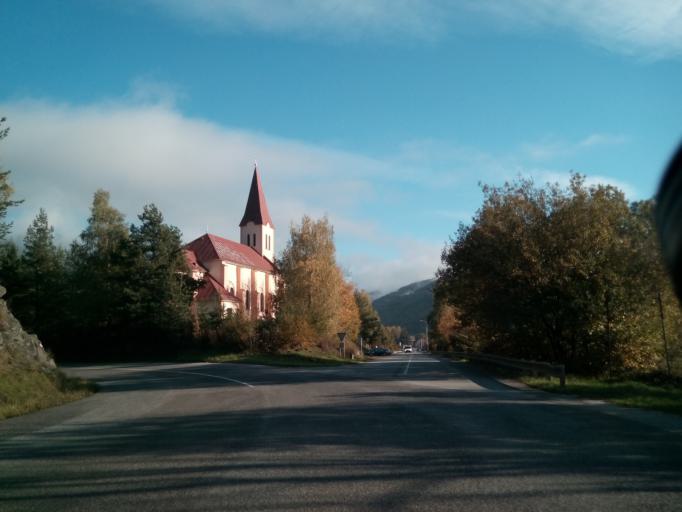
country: SK
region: Kosicky
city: Gelnica
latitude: 48.8873
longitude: 21.0062
